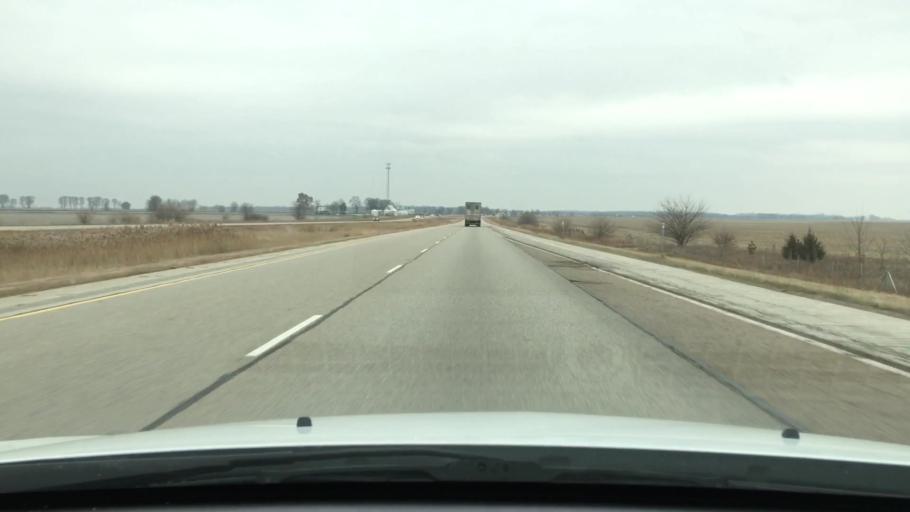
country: US
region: Illinois
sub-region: Logan County
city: Atlanta
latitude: 40.3167
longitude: -89.1594
